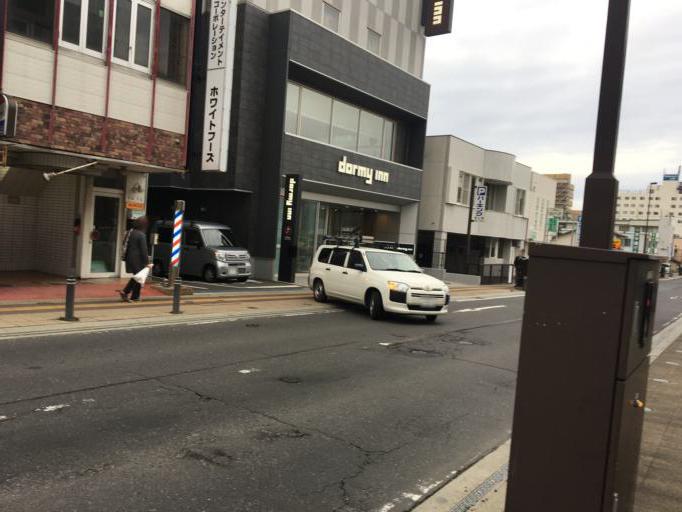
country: JP
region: Aomori
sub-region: Hachinohe Shi
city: Uchimaru
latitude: 40.5097
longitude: 141.4924
